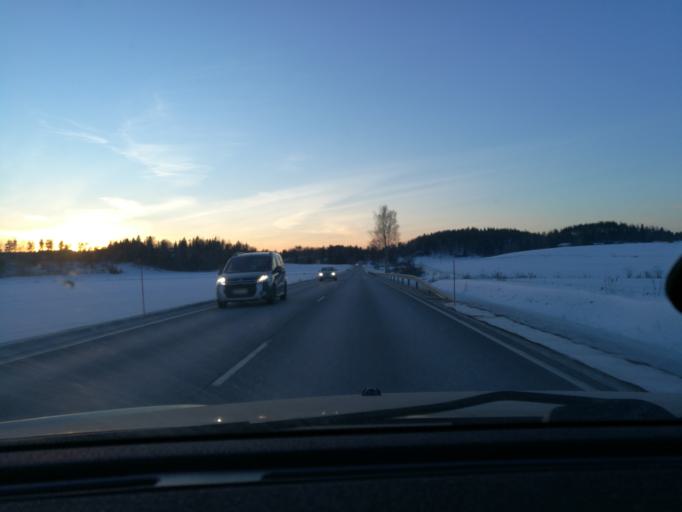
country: FI
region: Uusimaa
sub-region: Helsinki
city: Vihti
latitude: 60.4377
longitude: 24.3975
